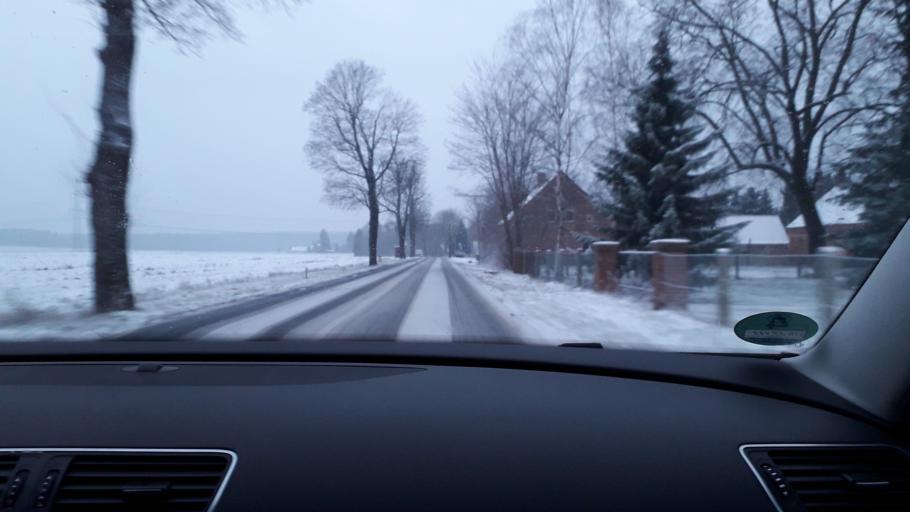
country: DE
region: Brandenburg
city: Spremberg
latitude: 51.5975
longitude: 14.4490
